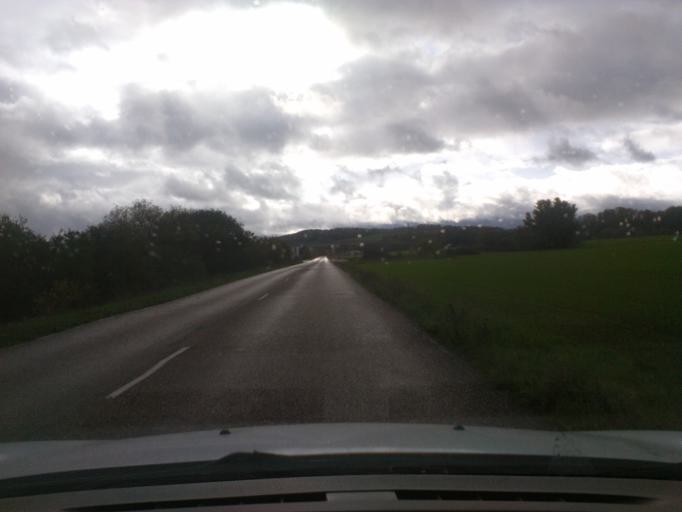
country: FR
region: Lorraine
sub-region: Departement des Vosges
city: Charmes
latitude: 48.3837
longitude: 6.2651
